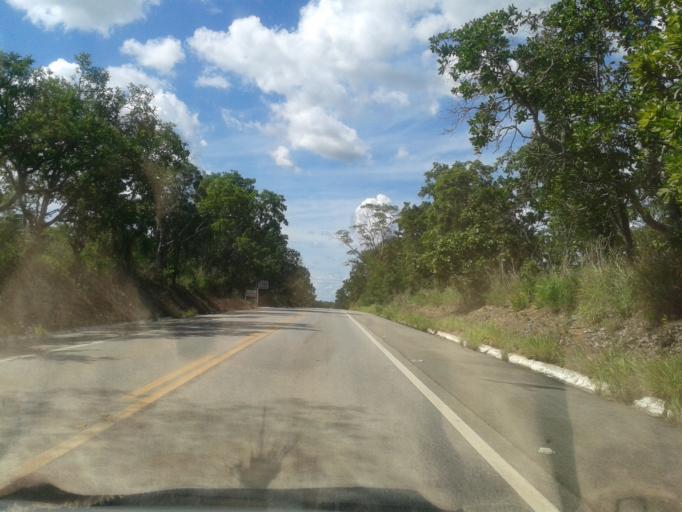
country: BR
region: Goias
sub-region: Itapuranga
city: Itapuranga
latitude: -15.5331
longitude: -50.2929
